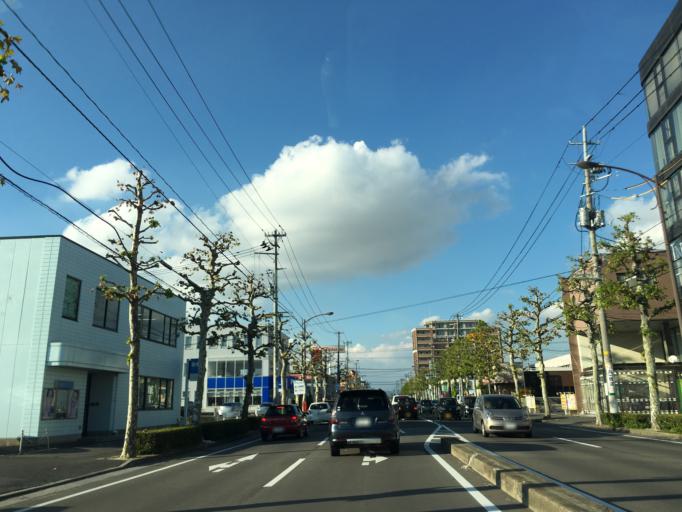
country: JP
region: Fukushima
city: Koriyama
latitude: 37.4050
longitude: 140.3623
